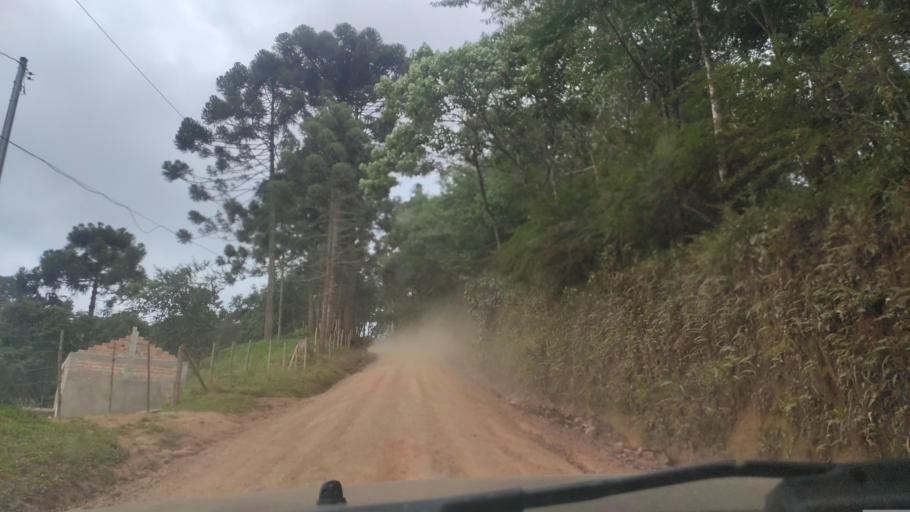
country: BR
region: Minas Gerais
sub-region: Paraisopolis
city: Paraisopolis
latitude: -22.6602
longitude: -45.8613
